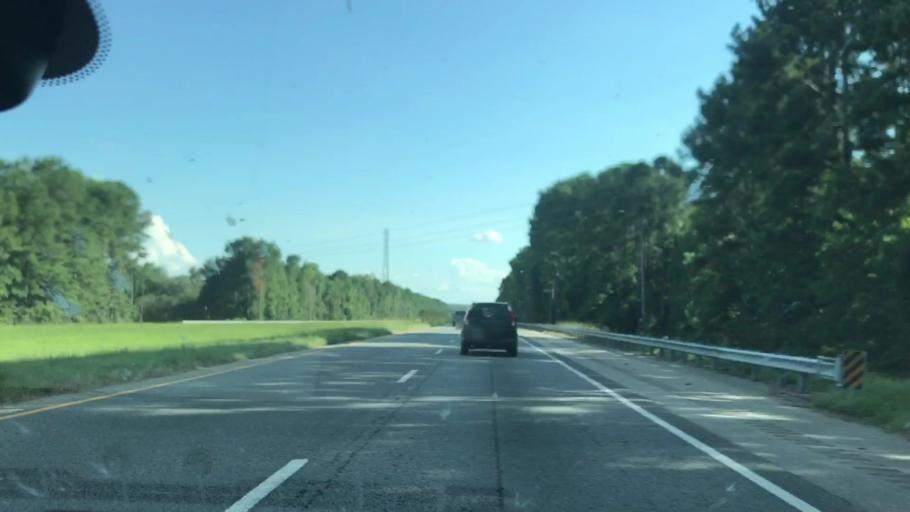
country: US
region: Georgia
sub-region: Harris County
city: Pine Mountain
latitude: 32.9184
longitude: -84.9472
